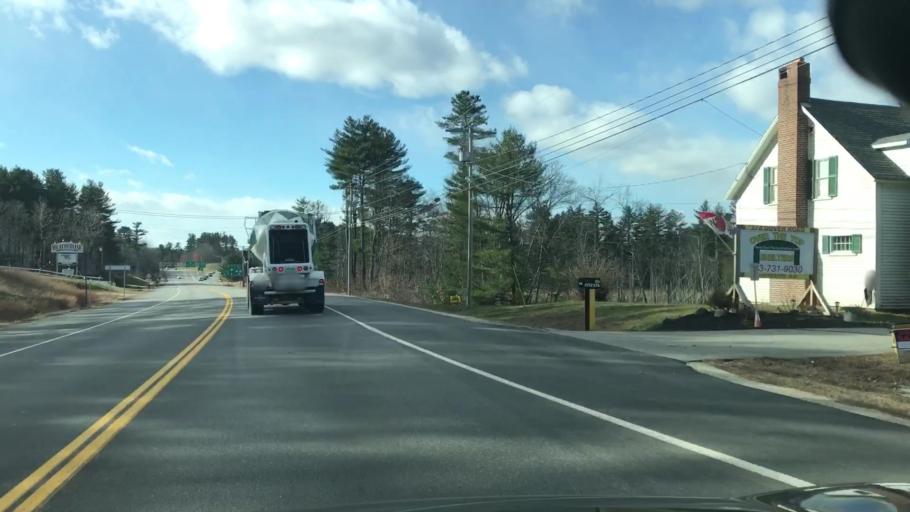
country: US
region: New Hampshire
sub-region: Merrimack County
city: Chichester
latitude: 43.2446
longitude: -71.4459
